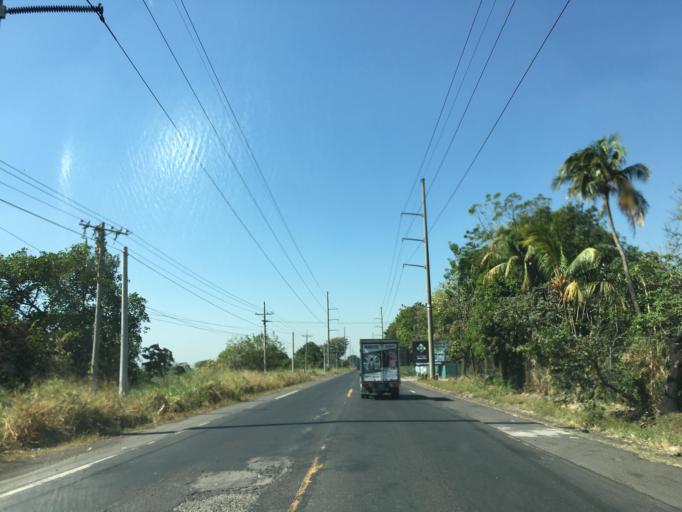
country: GT
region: Escuintla
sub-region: Municipio de Escuintla
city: Escuintla
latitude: 14.2575
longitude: -90.7996
